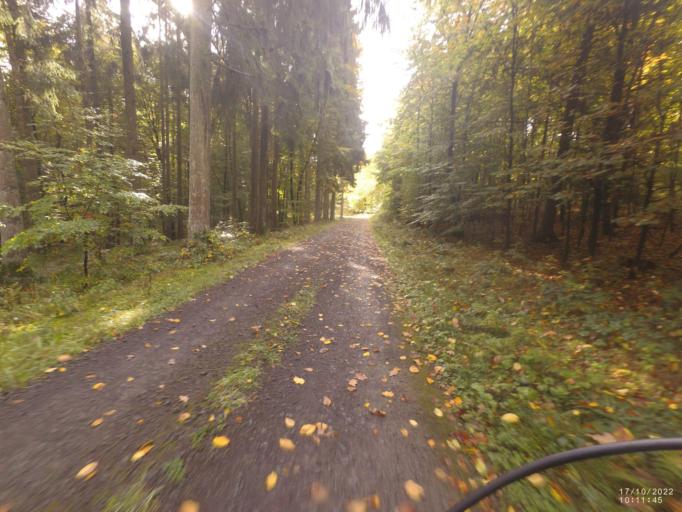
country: DE
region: Rheinland-Pfalz
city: Steiningen
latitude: 50.2063
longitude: 6.9116
